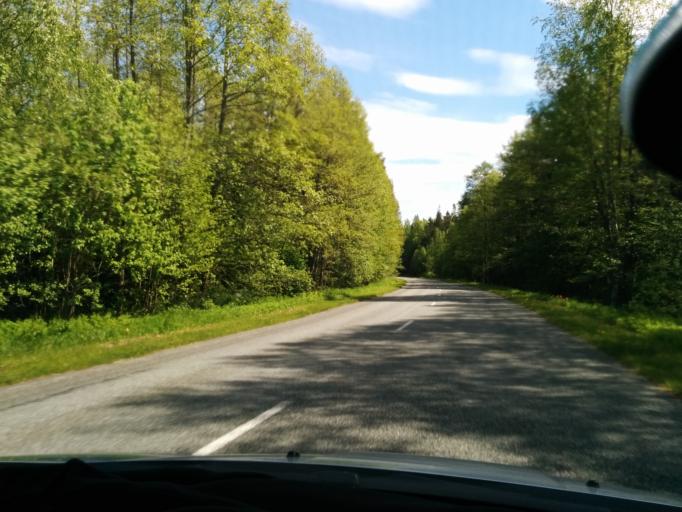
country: EE
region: Harju
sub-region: Loksa linn
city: Loksa
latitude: 59.5625
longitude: 25.9614
